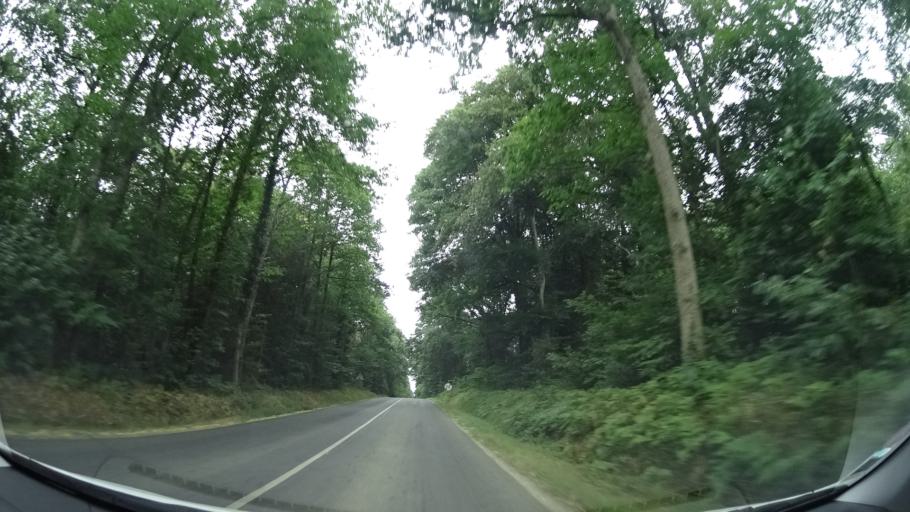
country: FR
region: Brittany
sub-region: Departement d'Ille-et-Vilaine
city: Pleugueneuc
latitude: 48.3512
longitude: -1.9248
